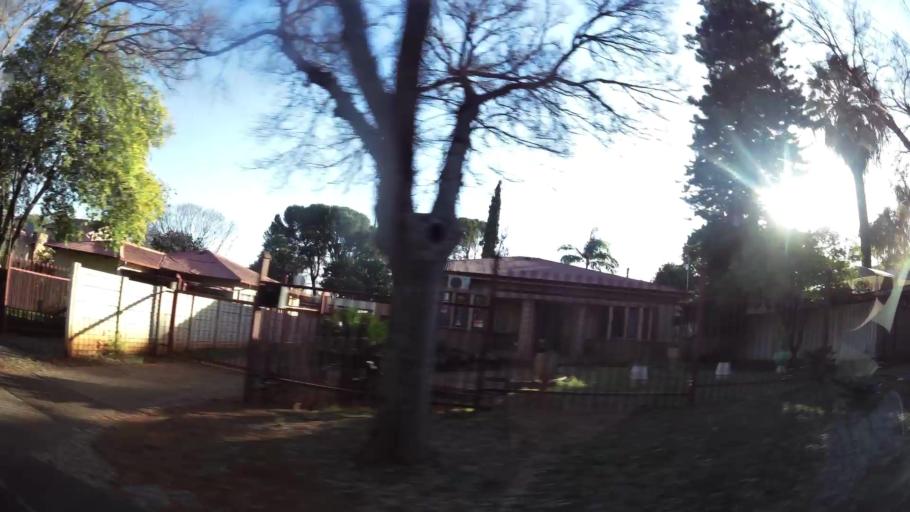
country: ZA
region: Gauteng
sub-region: City of Tshwane Metropolitan Municipality
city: Pretoria
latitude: -25.6994
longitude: 28.2041
